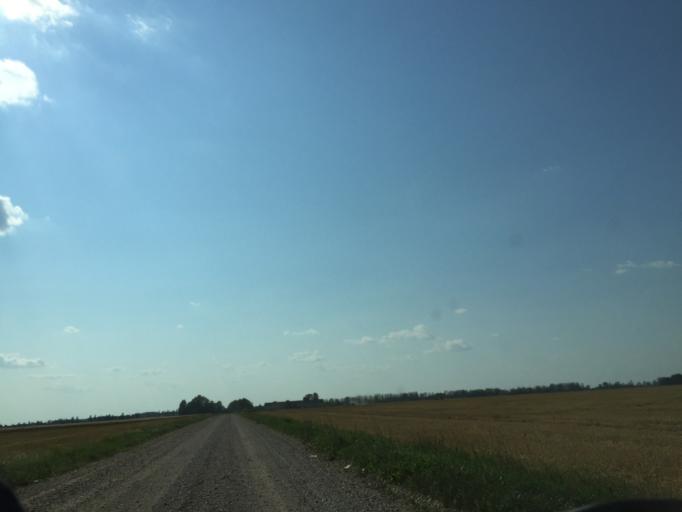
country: LV
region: Jelgava
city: Jelgava
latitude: 56.4549
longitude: 23.7155
